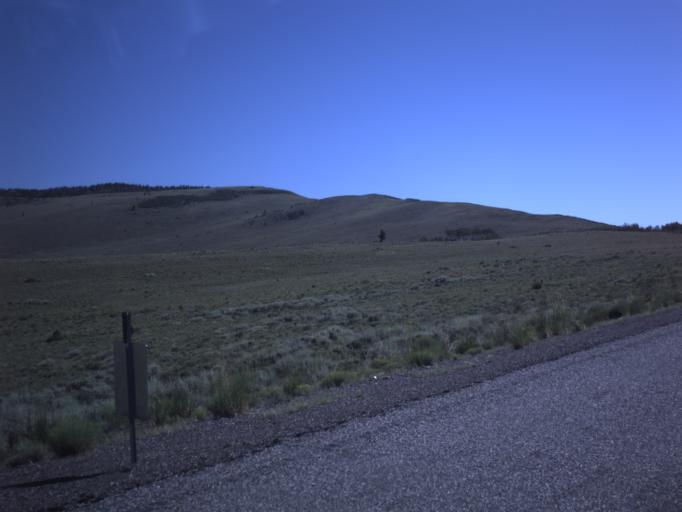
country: US
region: Utah
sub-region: Wayne County
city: Loa
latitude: 38.5790
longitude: -111.4848
